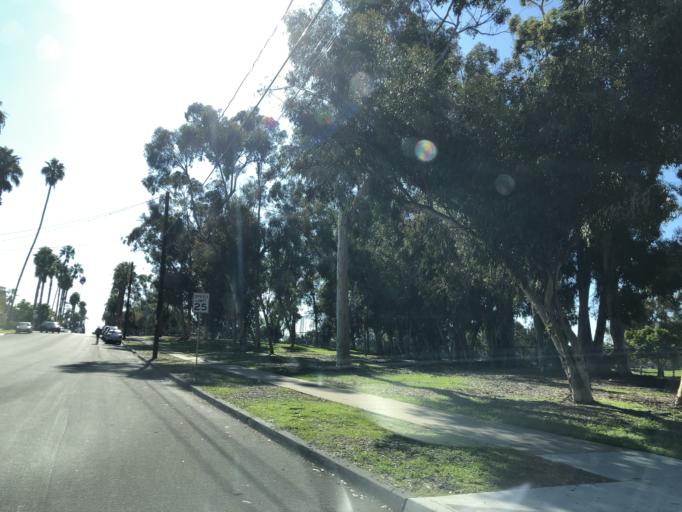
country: US
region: California
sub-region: San Diego County
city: San Diego
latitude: 32.7234
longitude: -117.1339
